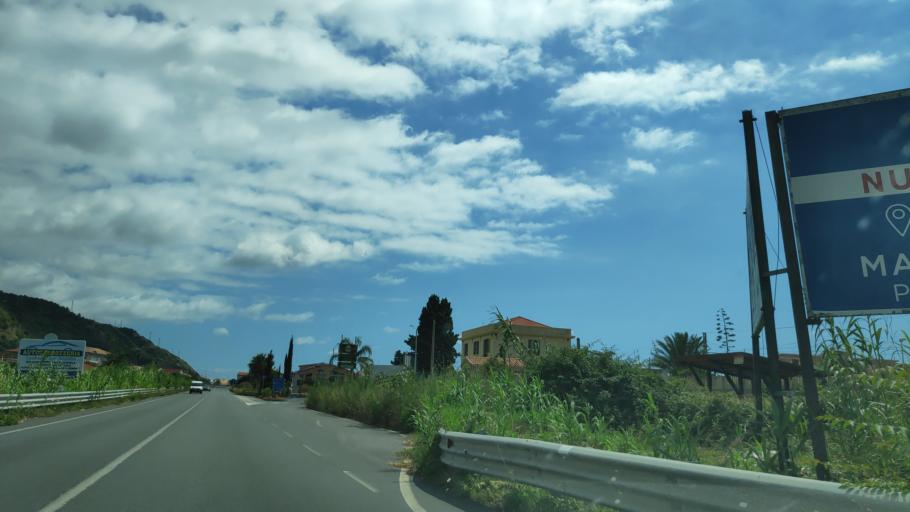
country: IT
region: Calabria
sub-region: Provincia di Cosenza
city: Belmonte Calabro
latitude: 39.1653
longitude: 16.0651
